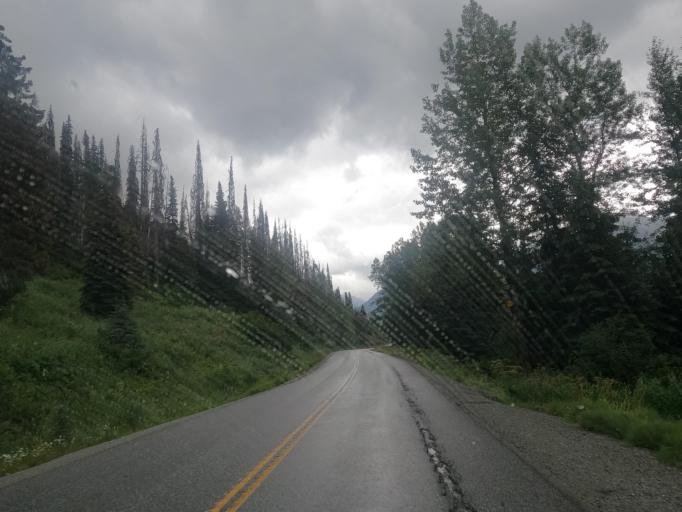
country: CA
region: British Columbia
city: Pemberton
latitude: 50.3856
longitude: -122.4442
